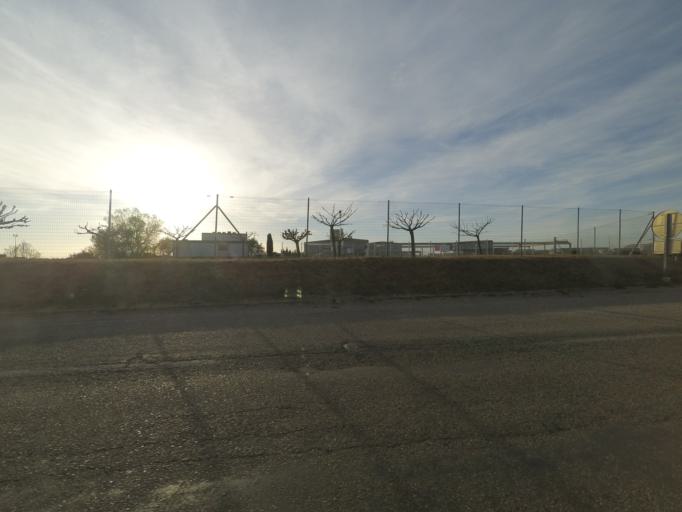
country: FR
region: Languedoc-Roussillon
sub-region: Departement du Gard
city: Codognan
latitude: 43.7177
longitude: 4.2265
